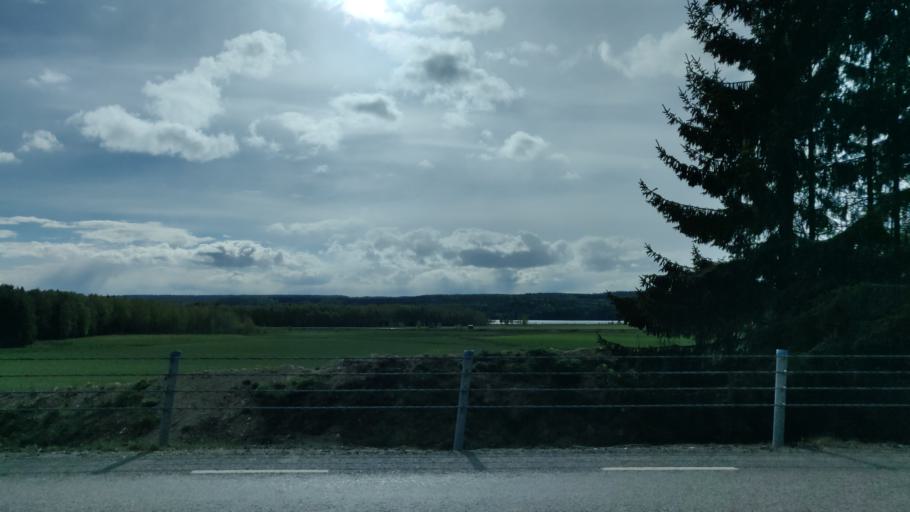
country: SE
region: Vaermland
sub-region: Forshaga Kommun
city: Deje
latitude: 59.5870
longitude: 13.4597
